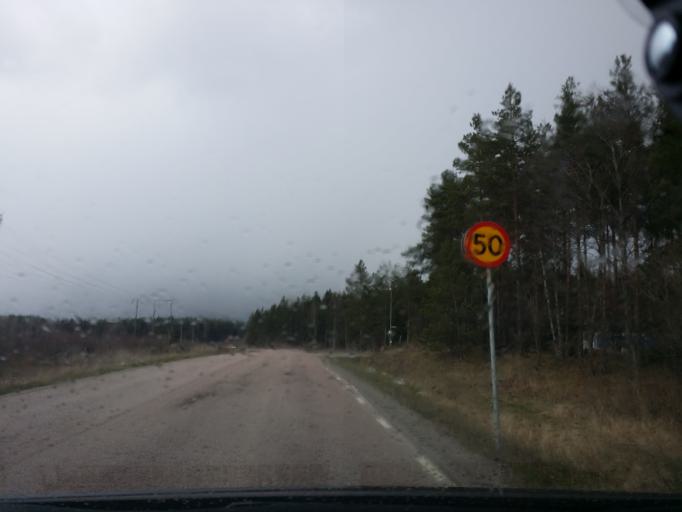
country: SE
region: Uppsala
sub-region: Enkopings Kommun
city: Enkoping
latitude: 59.6401
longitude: 17.1437
